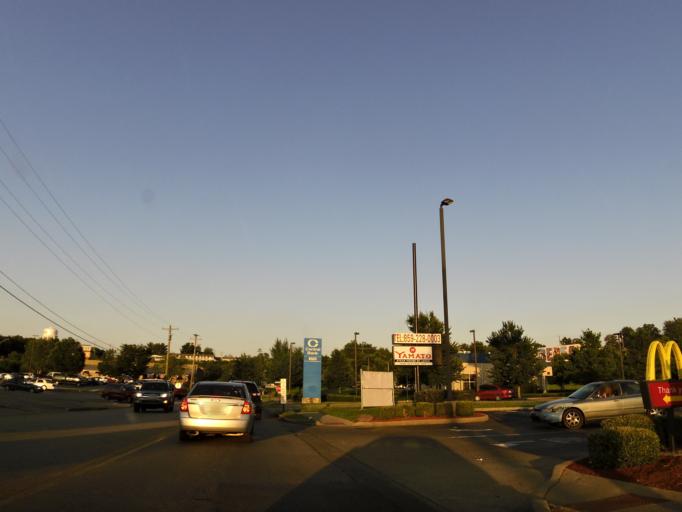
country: US
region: Kentucky
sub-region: Madison County
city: Berea
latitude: 37.5678
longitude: -84.3119
